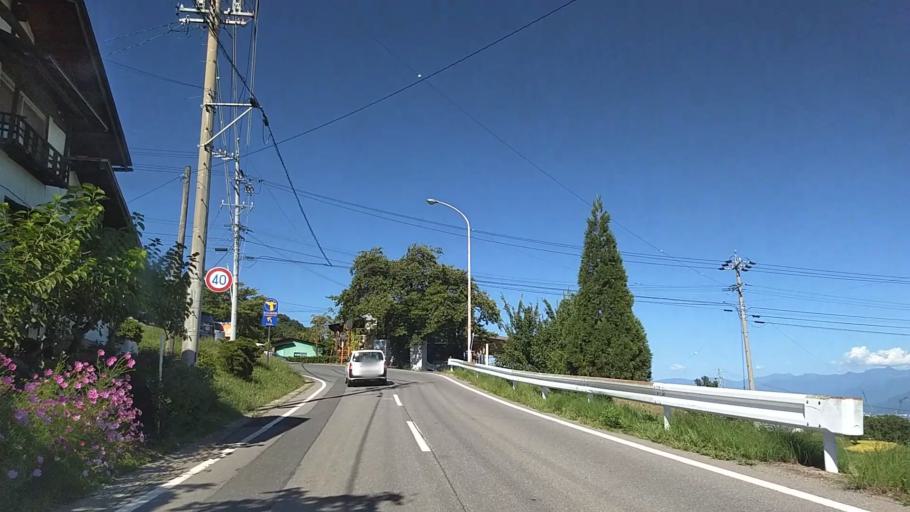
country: JP
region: Nagano
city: Nagano-shi
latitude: 36.5787
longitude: 138.1140
